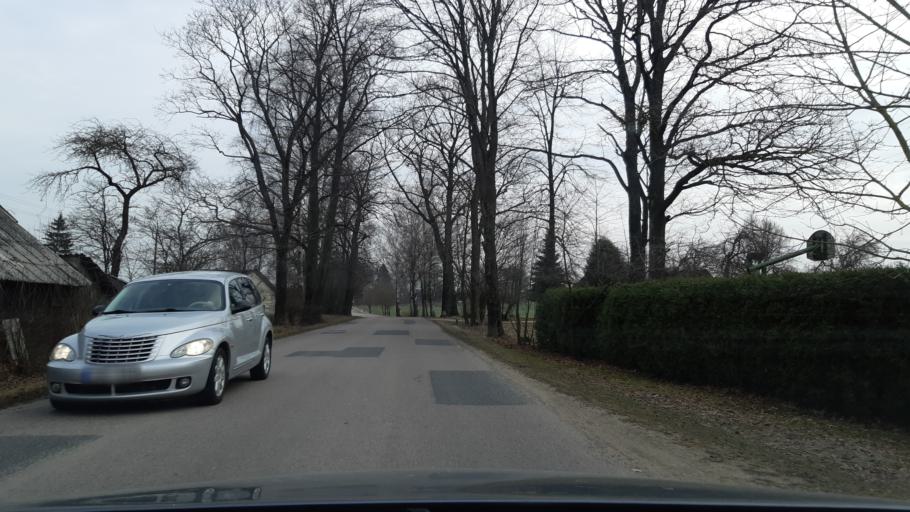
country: LT
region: Marijampoles apskritis
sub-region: Marijampole Municipality
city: Marijampole
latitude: 54.7180
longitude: 23.3249
